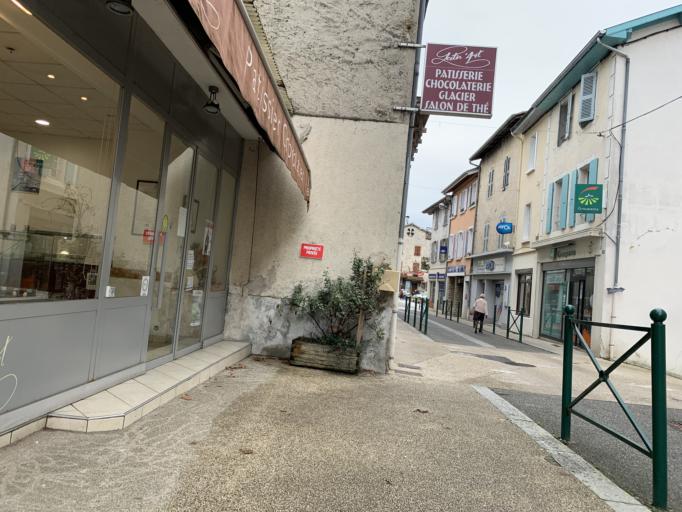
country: FR
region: Rhone-Alpes
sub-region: Departement de la Drome
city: Saint-Jean-en-Royans
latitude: 45.0174
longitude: 5.2923
